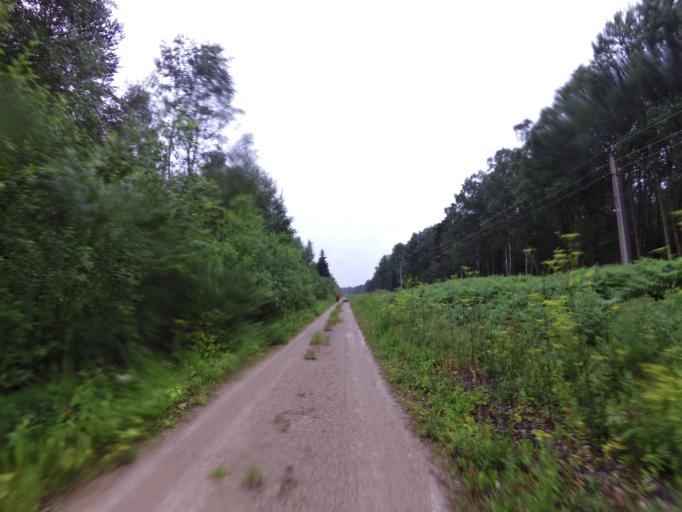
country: EE
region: Laeaene
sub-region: Lihula vald
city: Lihula
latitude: 58.9811
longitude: 23.9163
